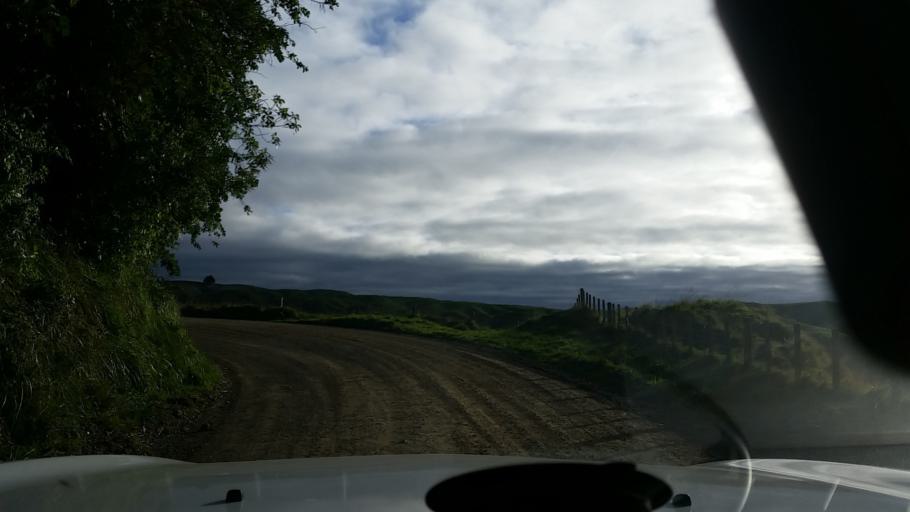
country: NZ
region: Hawke's Bay
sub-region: Napier City
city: Napier
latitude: -39.2618
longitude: 176.8518
